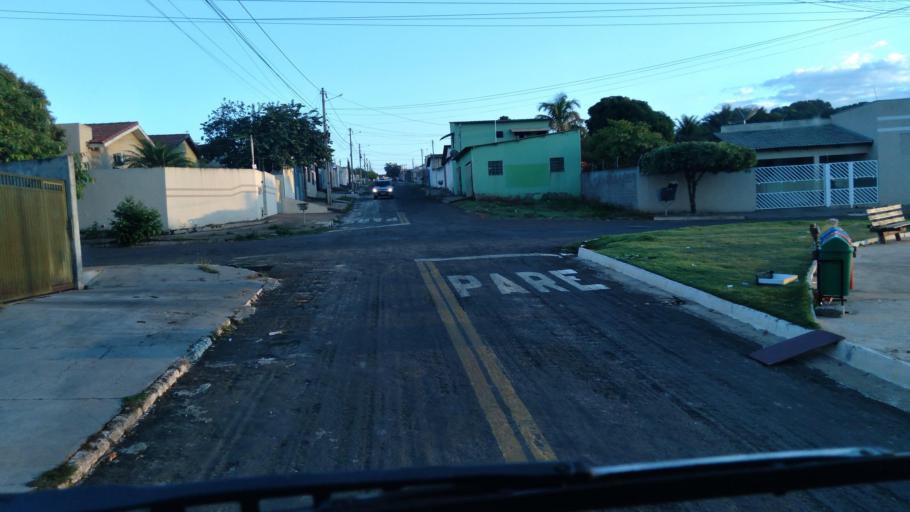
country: BR
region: Goias
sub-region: Mineiros
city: Mineiros
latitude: -17.5718
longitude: -52.5714
